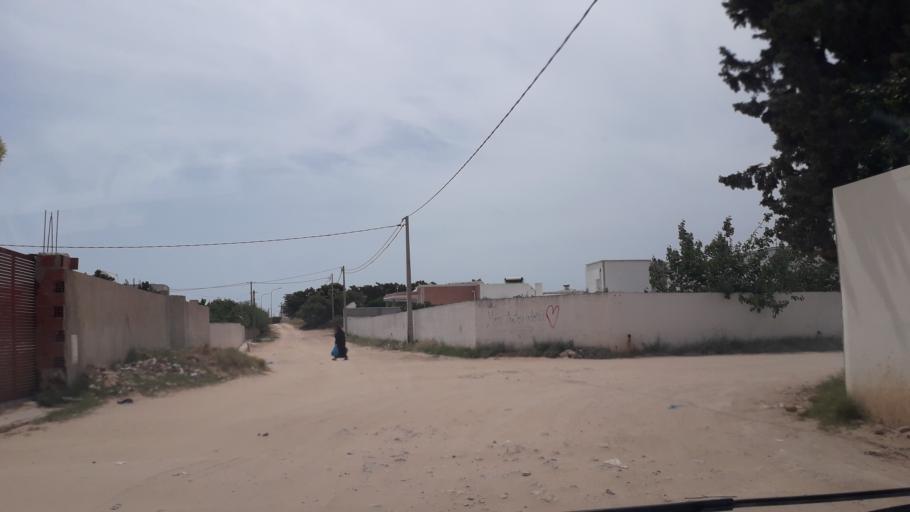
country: TN
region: Safaqis
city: Al Qarmadah
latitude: 34.8061
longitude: 10.7708
